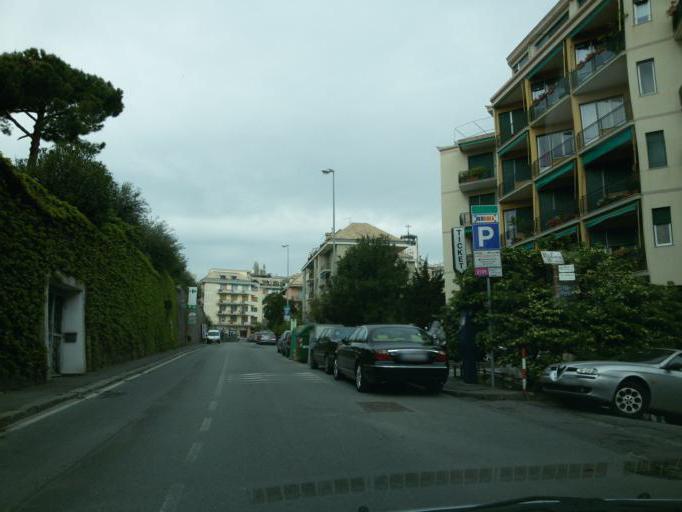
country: IT
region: Liguria
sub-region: Provincia di Genova
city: Genoa
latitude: 44.3985
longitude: 8.9759
